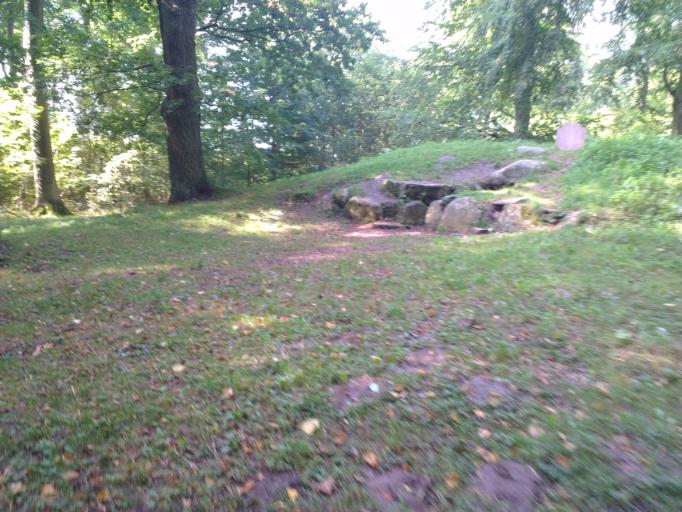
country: DK
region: Capital Region
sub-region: Frederikssund Kommune
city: Jaegerspris
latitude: 55.8608
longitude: 11.9835
